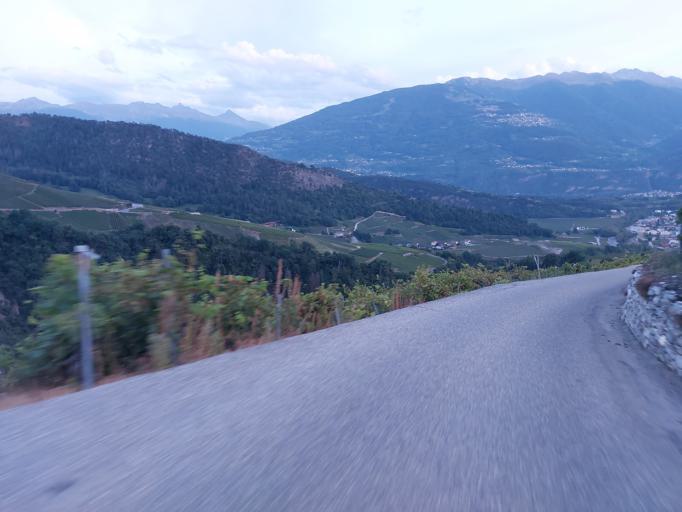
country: CH
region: Valais
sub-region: Conthey District
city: Conthey
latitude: 46.2465
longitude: 7.3072
